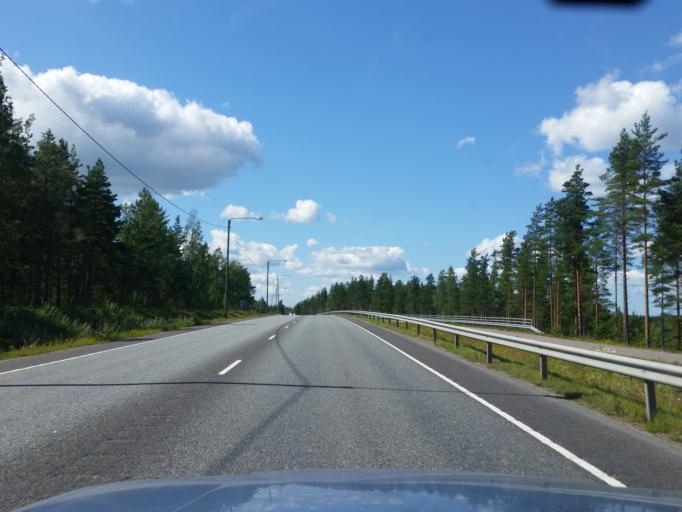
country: FI
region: Uusimaa
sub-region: Helsinki
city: Vihti
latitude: 60.3232
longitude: 24.2697
